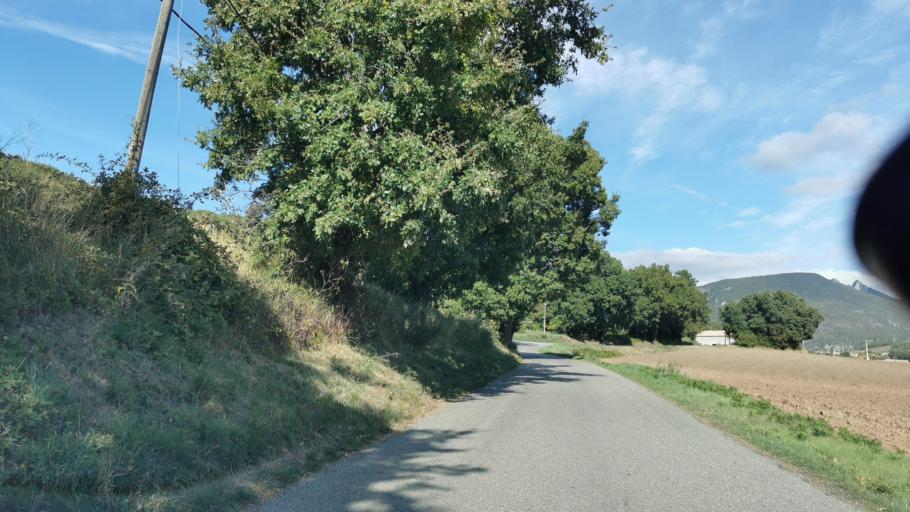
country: FR
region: Provence-Alpes-Cote d'Azur
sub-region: Departement des Alpes-de-Haute-Provence
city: Sisteron
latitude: 44.1712
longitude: 5.9681
